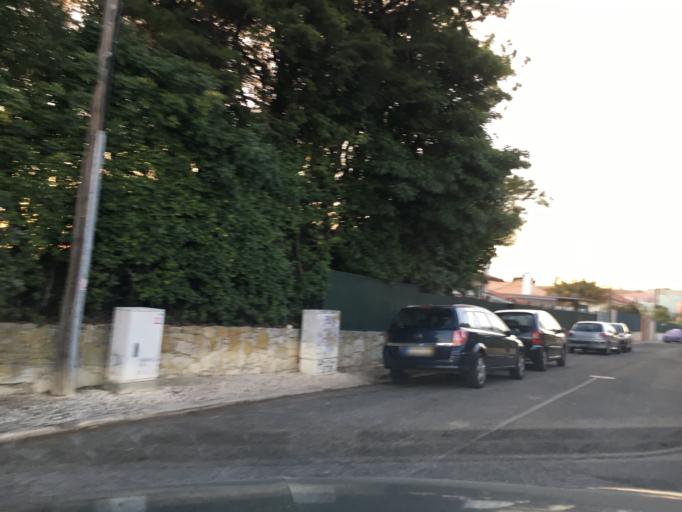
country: PT
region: Lisbon
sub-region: Oeiras
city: Paco de Arcos
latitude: 38.7002
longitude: -9.2893
